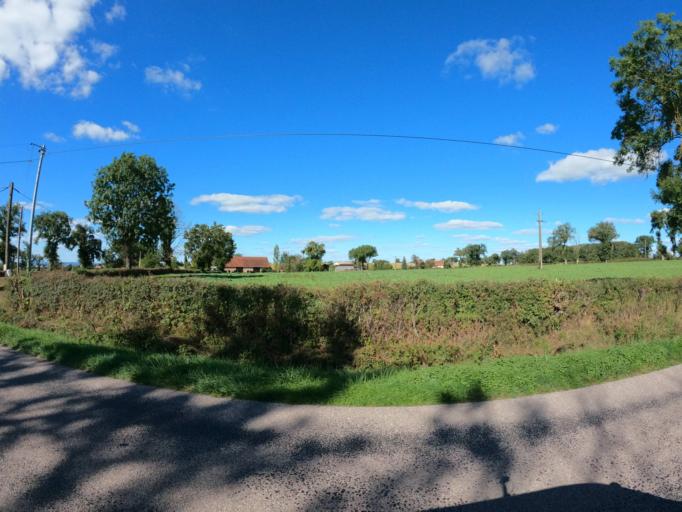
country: FR
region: Auvergne
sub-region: Departement de l'Allier
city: Buxieres-les-Mines
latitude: 46.4048
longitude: 2.9672
